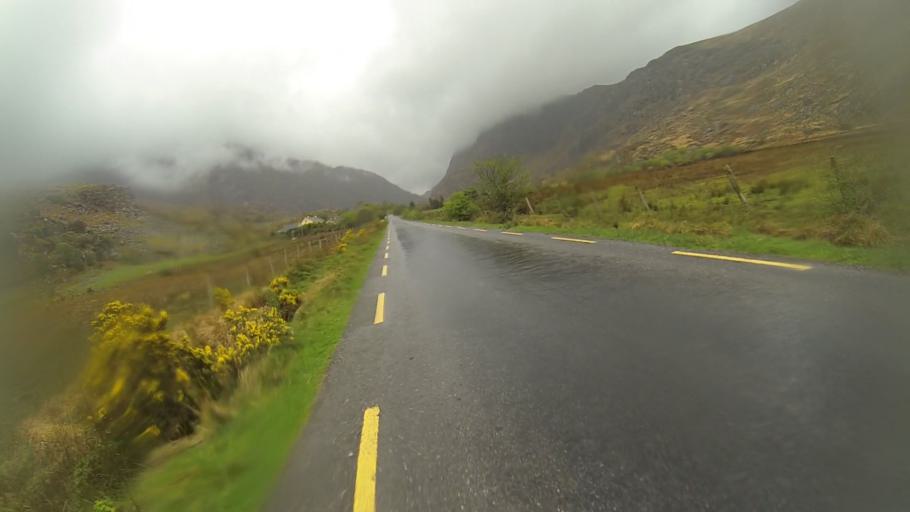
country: IE
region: Munster
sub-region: Ciarrai
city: Cill Airne
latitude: 52.0258
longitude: -9.6356
